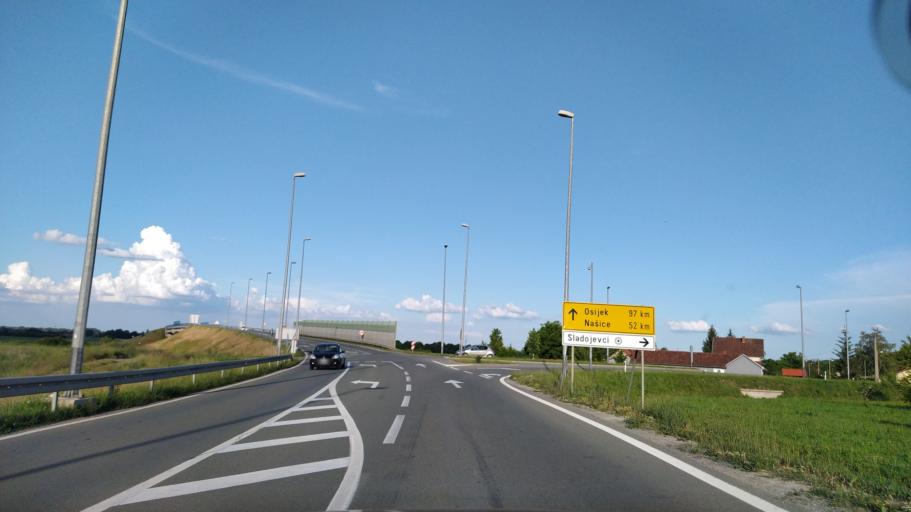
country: HR
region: Virovitick-Podravska
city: Slatina
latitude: 45.7249
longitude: 17.6387
